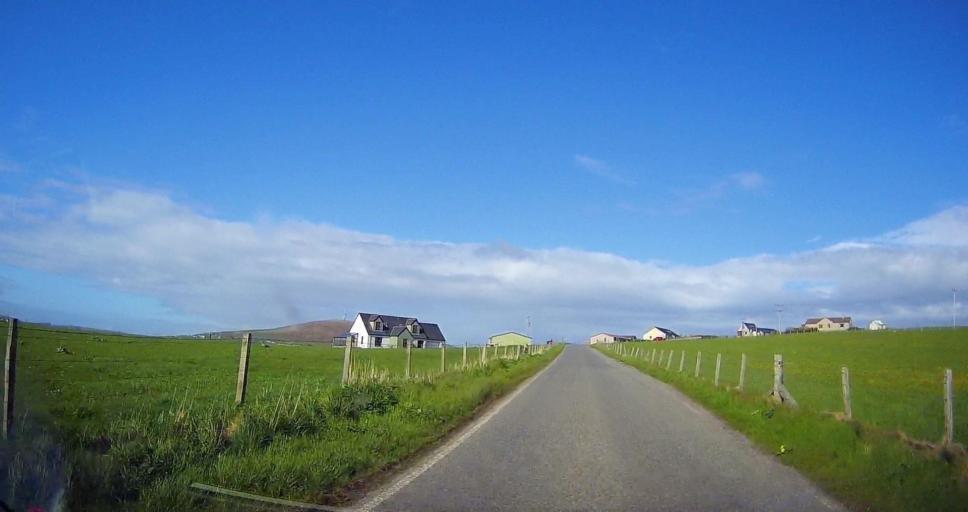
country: GB
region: Scotland
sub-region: Shetland Islands
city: Sandwick
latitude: 59.9148
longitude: -1.3227
